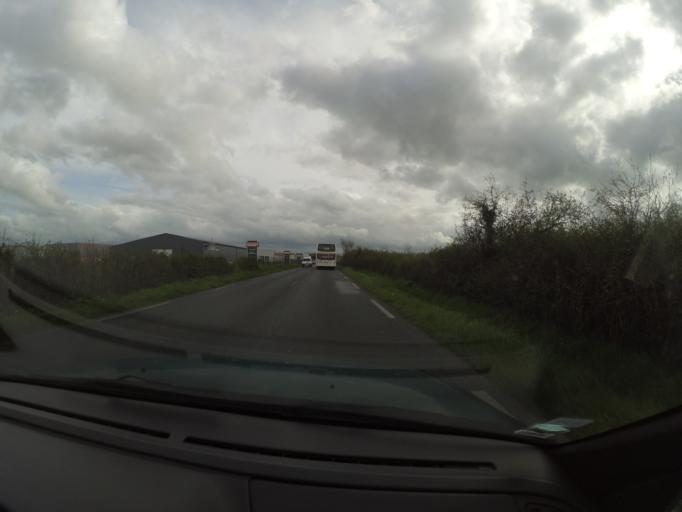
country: FR
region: Pays de la Loire
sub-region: Departement de Maine-et-Loire
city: Lire
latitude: 47.3242
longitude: -1.1659
